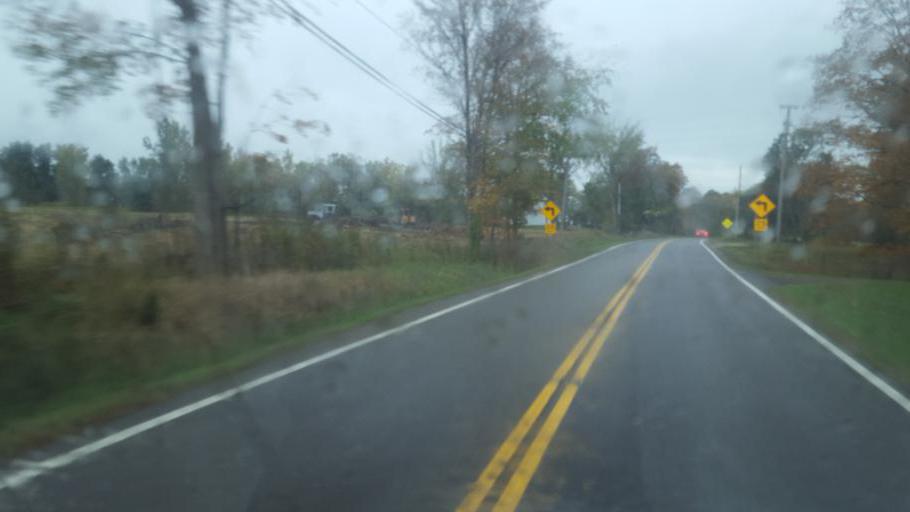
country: US
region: Ohio
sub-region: Richland County
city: Lincoln Heights
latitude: 40.8484
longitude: -82.4667
